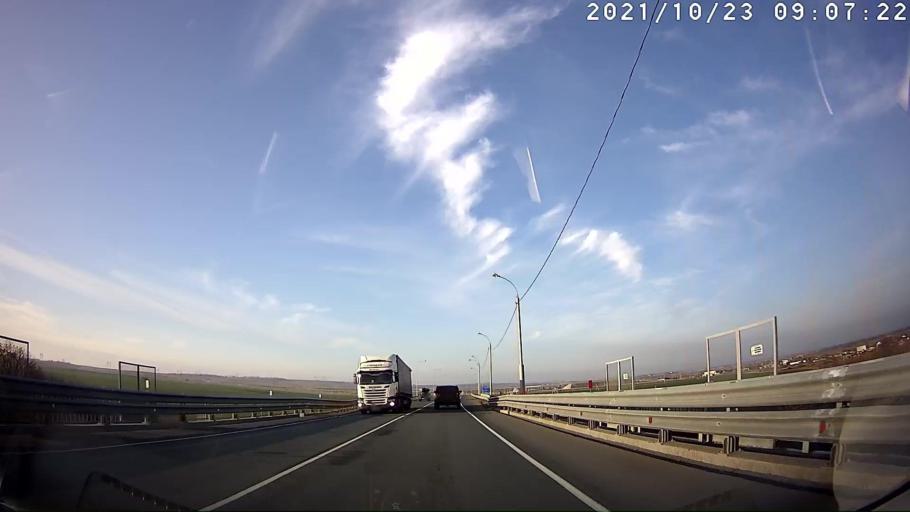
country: RU
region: Saratov
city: Yelshanka
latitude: 51.8005
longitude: 46.1871
